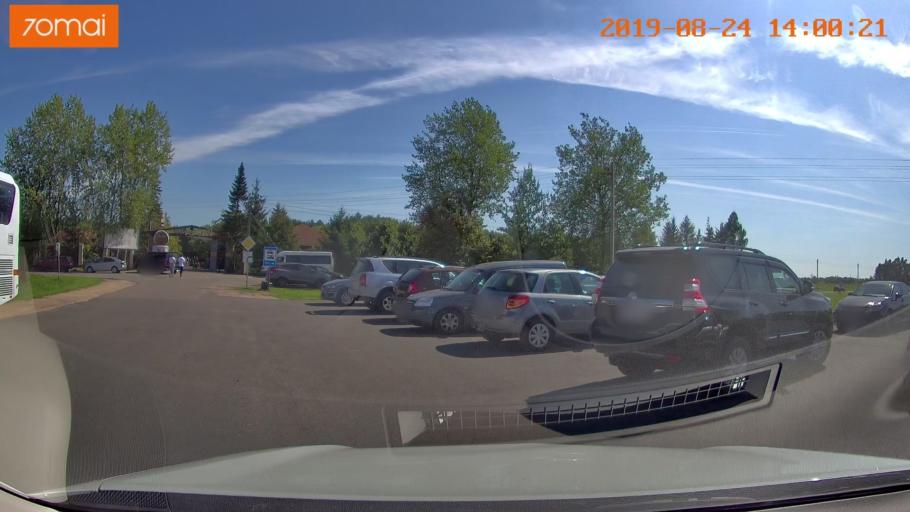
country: BY
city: Michanovichi
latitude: 53.5964
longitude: 27.6824
